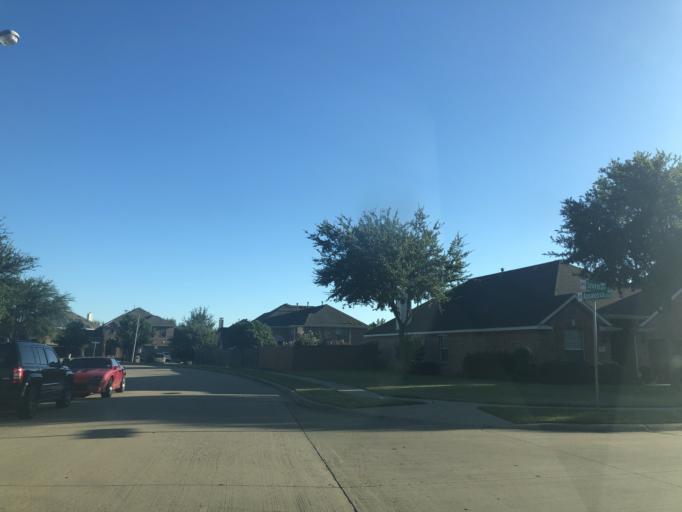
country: US
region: Texas
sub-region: Dallas County
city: Cedar Hill
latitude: 32.6550
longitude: -96.9990
